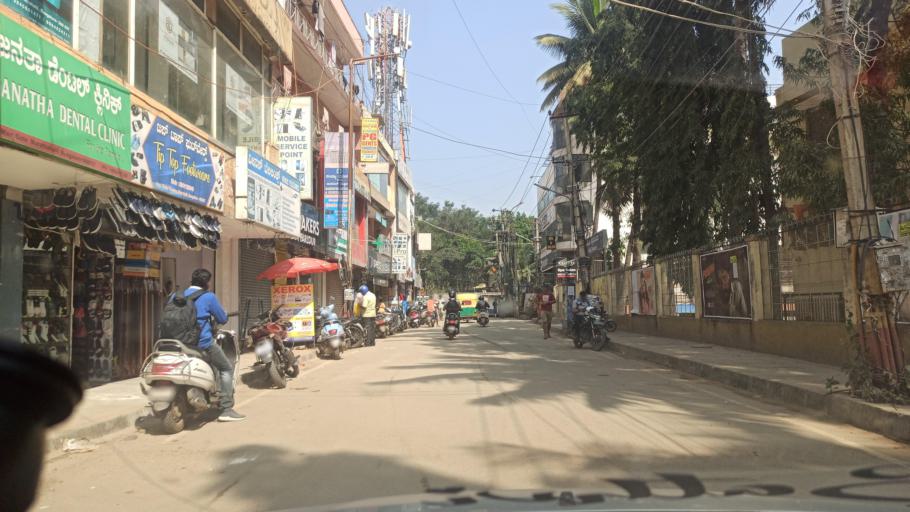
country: IN
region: Karnataka
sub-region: Bangalore Urban
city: Bangalore
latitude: 12.9562
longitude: 77.6979
